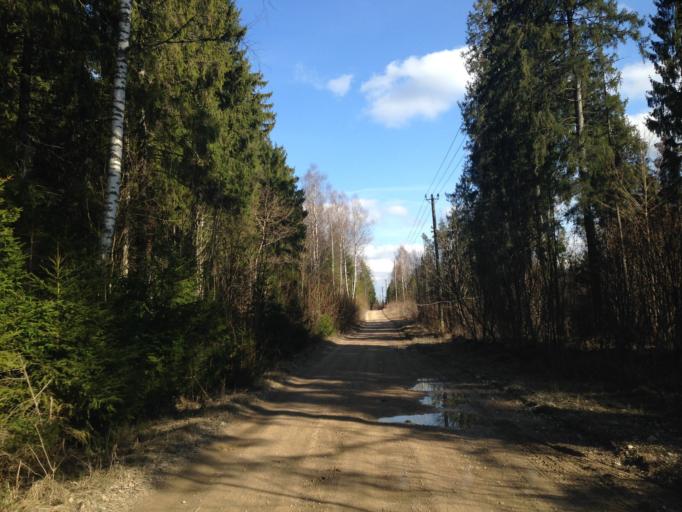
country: EE
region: Harju
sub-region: Keila linn
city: Keila
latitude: 59.1794
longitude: 24.4401
